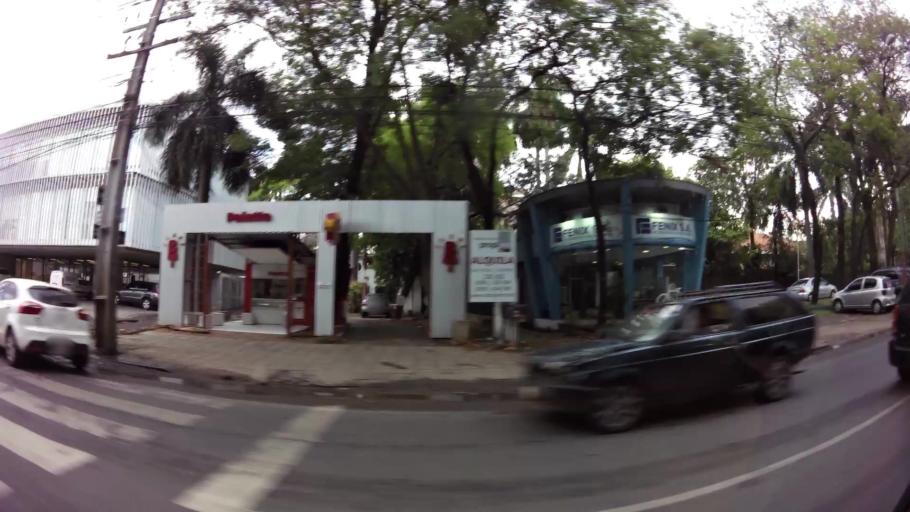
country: PY
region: Asuncion
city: Asuncion
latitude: -25.2858
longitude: -57.5756
